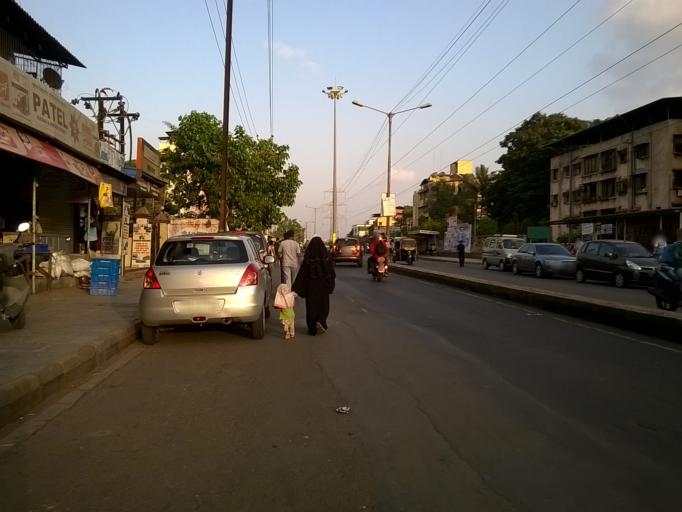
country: IN
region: Maharashtra
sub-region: Raigarh
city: Kalundri
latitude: 18.9900
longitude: 73.1255
